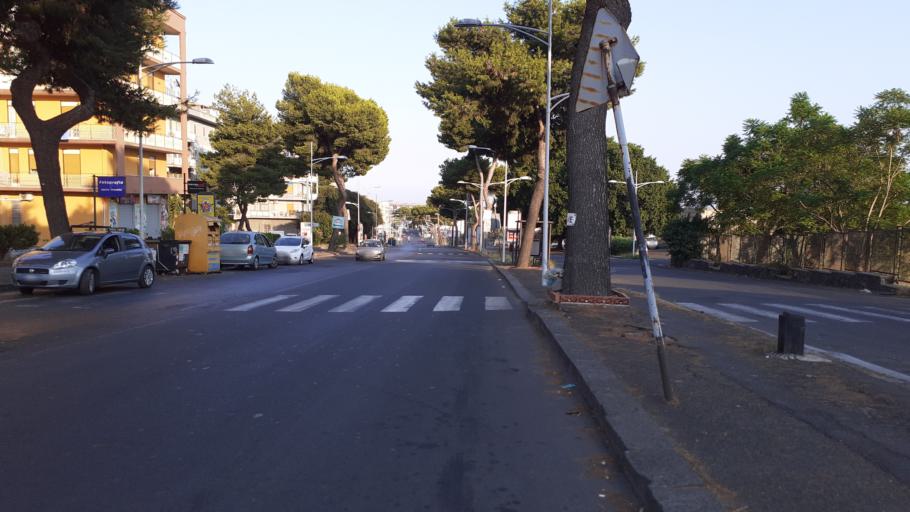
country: IT
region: Sicily
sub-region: Catania
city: Catania
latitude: 37.5059
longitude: 15.0531
